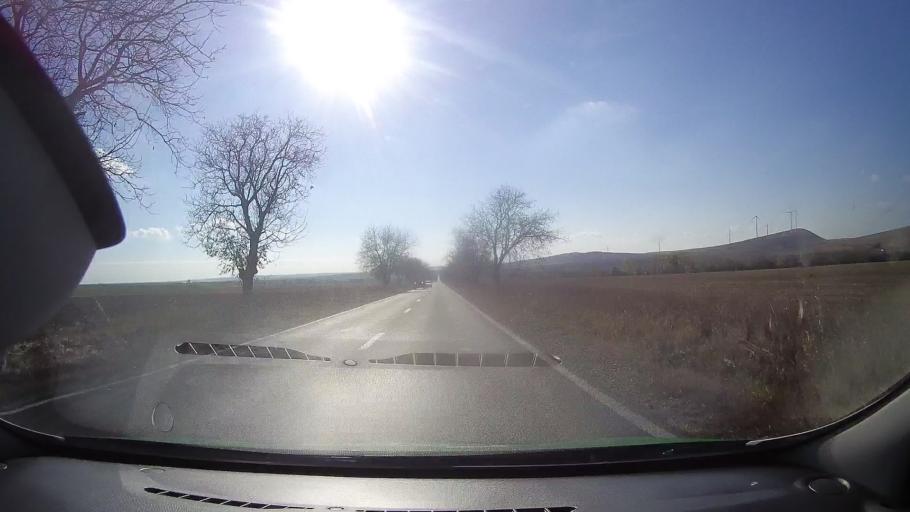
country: RO
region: Tulcea
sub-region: Comuna Ceamurlia de Jos
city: Ceamurlia de Jos
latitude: 44.7824
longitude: 28.6892
